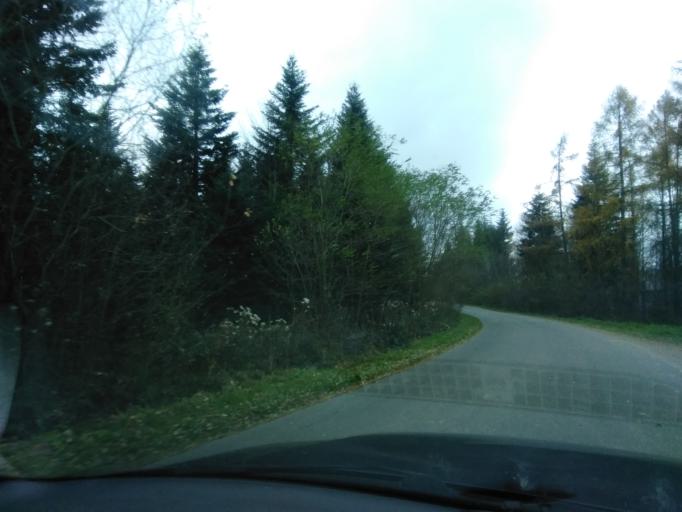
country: PL
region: Subcarpathian Voivodeship
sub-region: Powiat strzyzowski
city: Wysoka Strzyzowska
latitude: 49.8264
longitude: 21.7808
